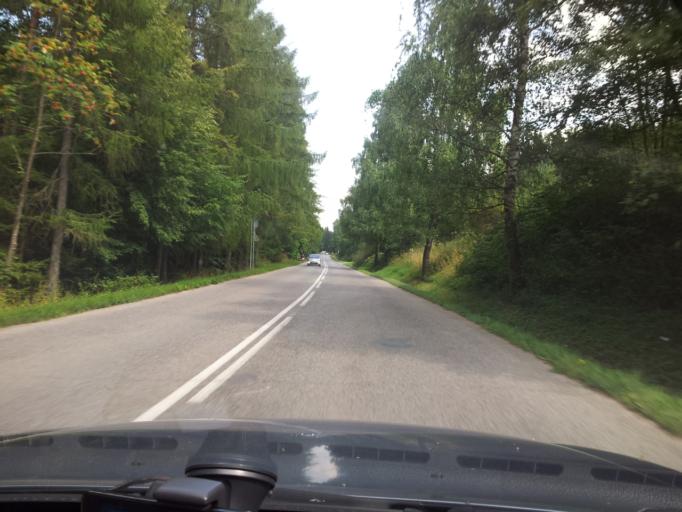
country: SK
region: Zilinsky
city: Namestovo
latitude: 49.3976
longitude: 19.4930
